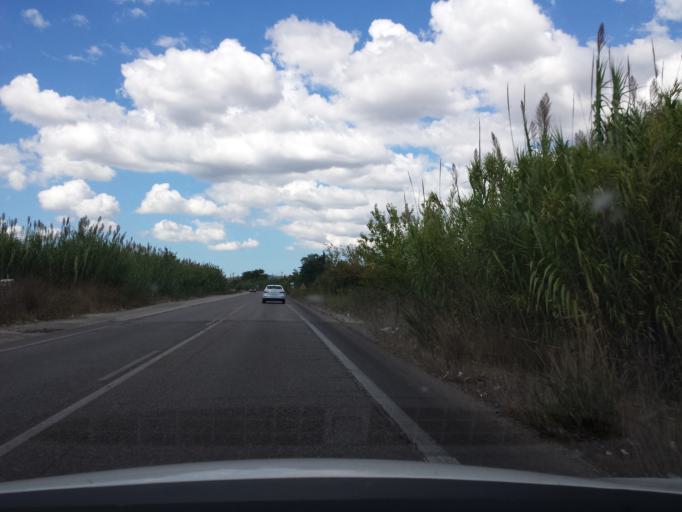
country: GR
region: West Greece
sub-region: Nomos Ileias
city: Pyrgos
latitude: 37.6613
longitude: 21.4616
